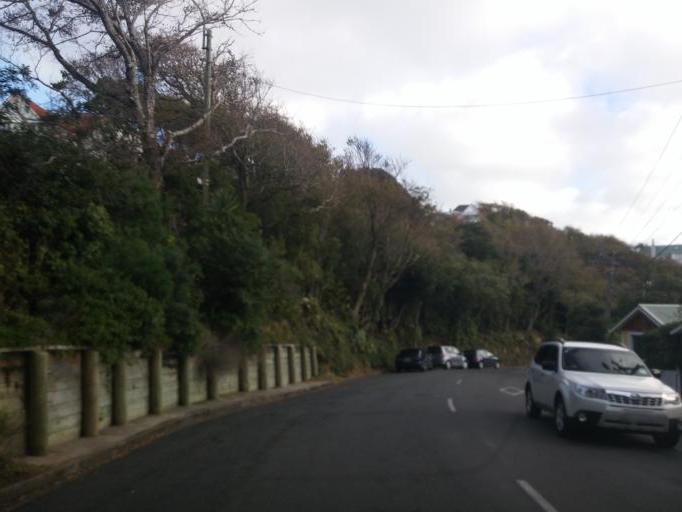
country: NZ
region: Wellington
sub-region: Wellington City
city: Kelburn
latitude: -41.2882
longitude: 174.7654
